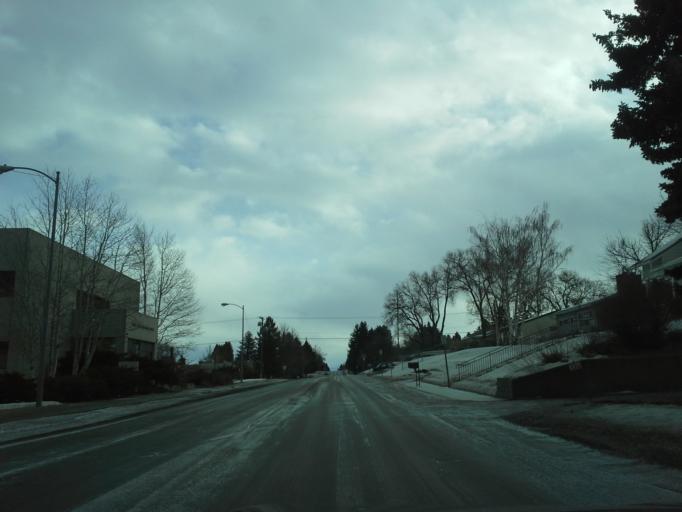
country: US
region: Montana
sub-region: Lewis and Clark County
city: Helena
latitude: 46.5841
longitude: -112.0164
